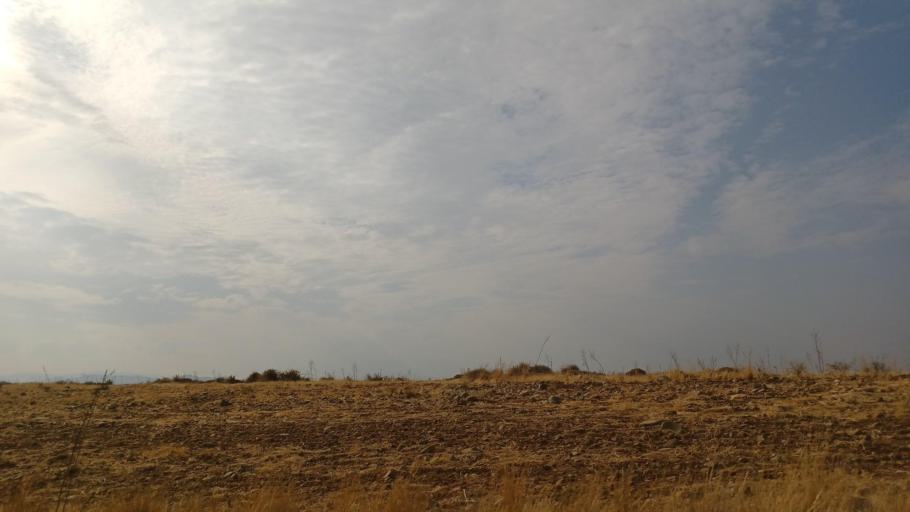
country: CY
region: Lefkosia
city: Peristerona
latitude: 35.0825
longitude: 33.0934
